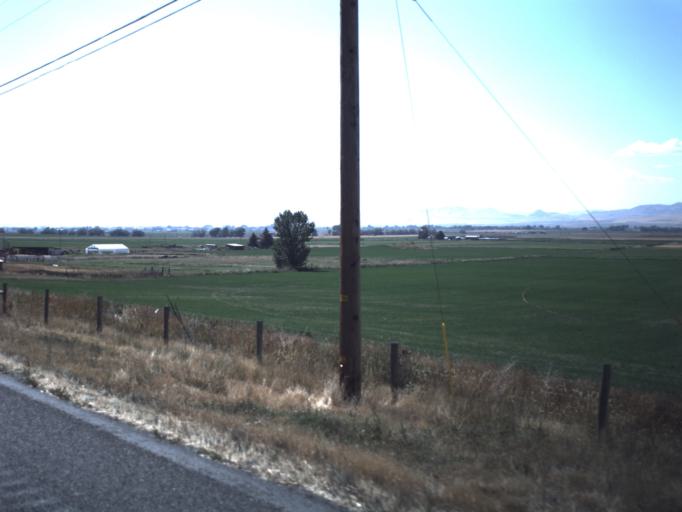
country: US
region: Utah
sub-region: Cache County
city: Richmond
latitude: 41.8831
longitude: -111.8197
